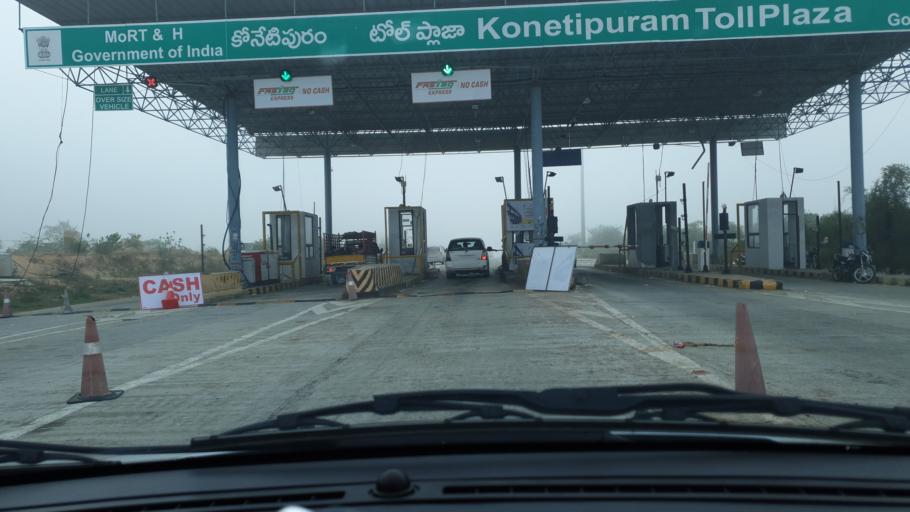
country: IN
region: Telangana
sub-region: Nalgonda
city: Devarkonda
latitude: 16.6123
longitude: 78.6758
